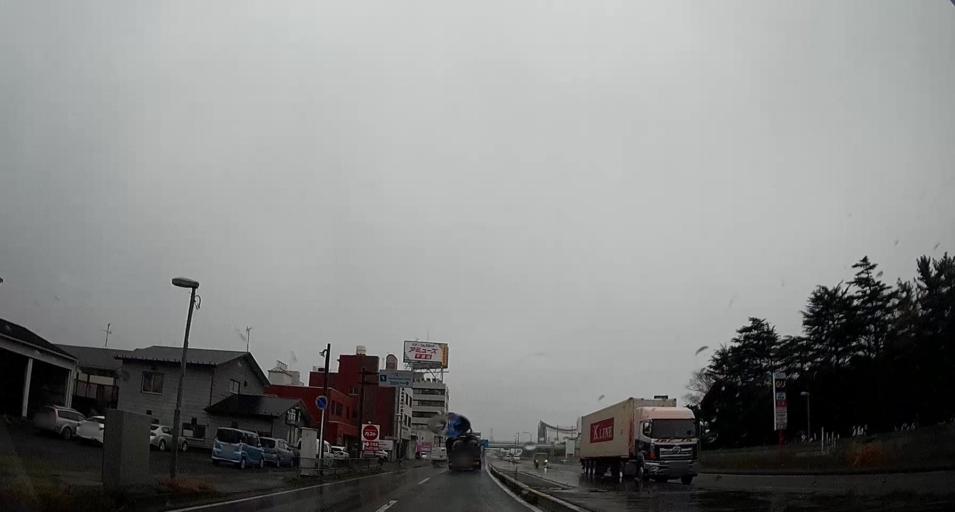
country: JP
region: Chiba
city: Chiba
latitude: 35.5825
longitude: 140.1259
